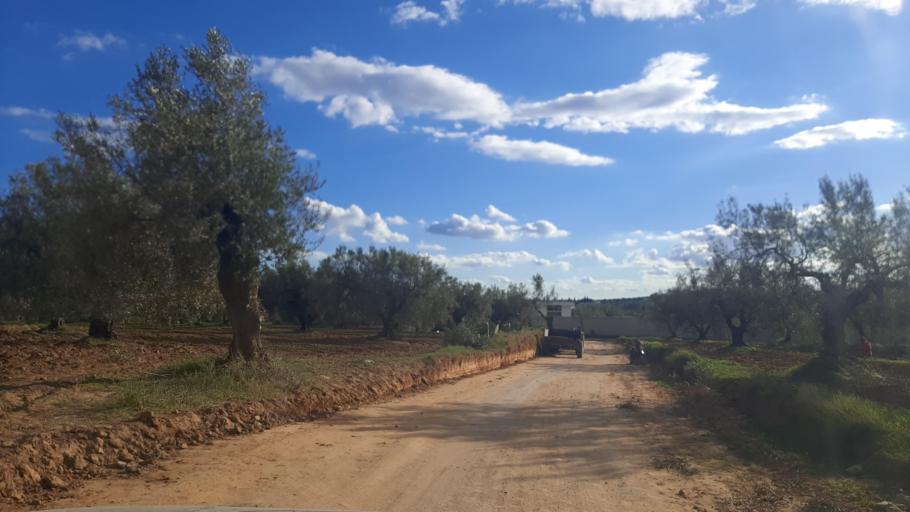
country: TN
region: Nabul
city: Al Hammamat
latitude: 36.4246
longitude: 10.5080
